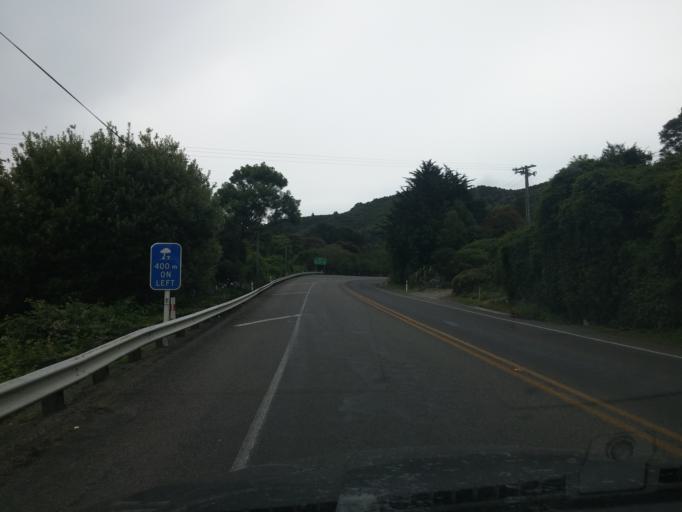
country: NZ
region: Wellington
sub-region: Upper Hutt City
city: Upper Hutt
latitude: -41.1150
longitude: 175.3156
